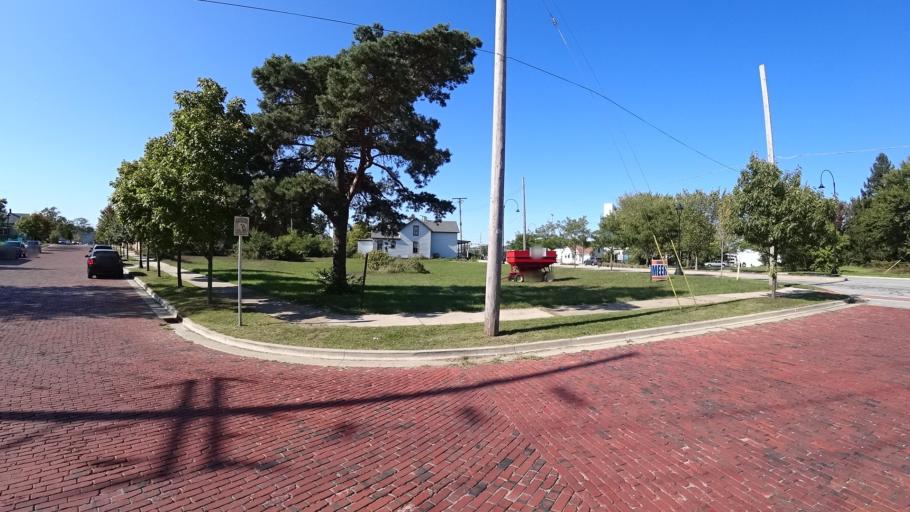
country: US
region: Indiana
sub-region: LaPorte County
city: Michigan City
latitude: 41.7147
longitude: -86.8908
